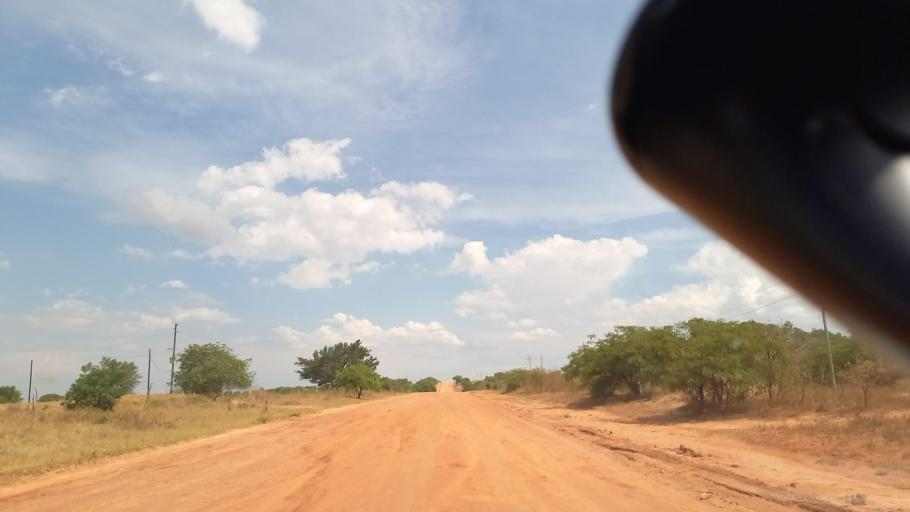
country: ZM
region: Lusaka
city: Kafue
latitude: -16.1252
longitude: 28.0434
